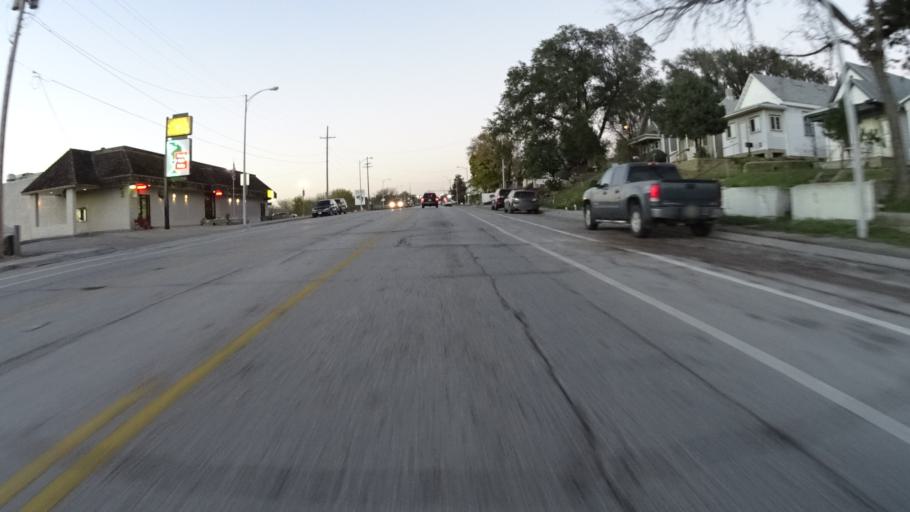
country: US
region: Nebraska
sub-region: Douglas County
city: Omaha
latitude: 41.2021
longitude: -95.9471
